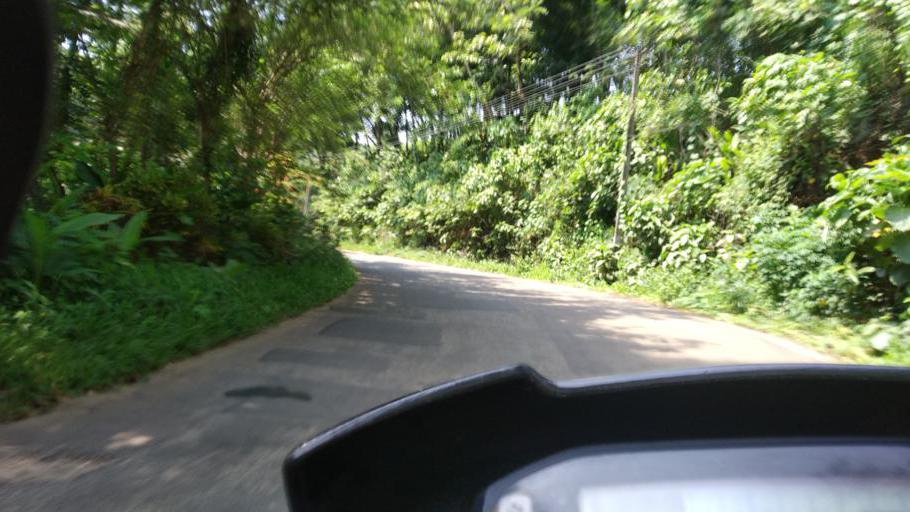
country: IN
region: Kerala
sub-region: Kottayam
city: Erattupetta
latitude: 9.6939
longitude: 76.8248
